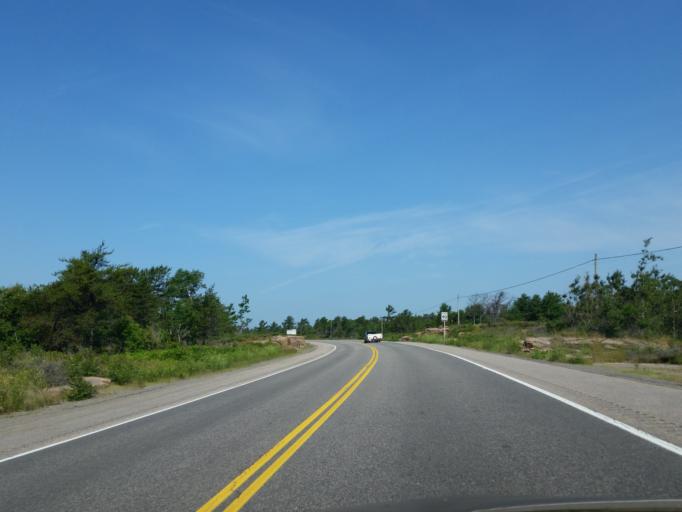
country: CA
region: Ontario
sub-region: Parry Sound District
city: Parry Sound
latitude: 45.7793
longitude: -80.5018
